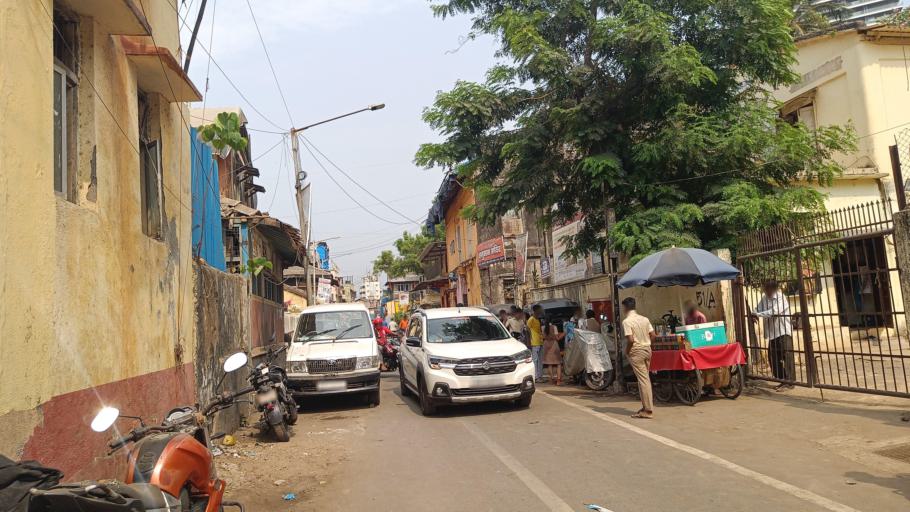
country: IN
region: Maharashtra
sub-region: Mumbai Suburban
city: Mumbai
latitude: 19.0540
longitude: 72.8343
